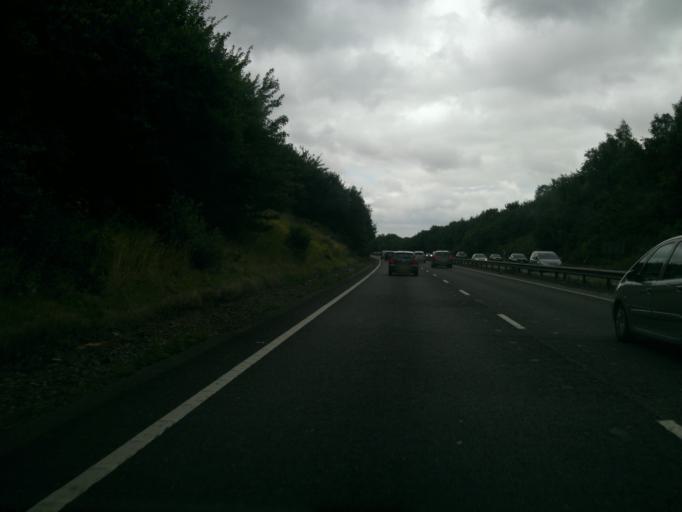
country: GB
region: England
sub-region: Essex
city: Great Horkesley
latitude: 51.9184
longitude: 0.8784
